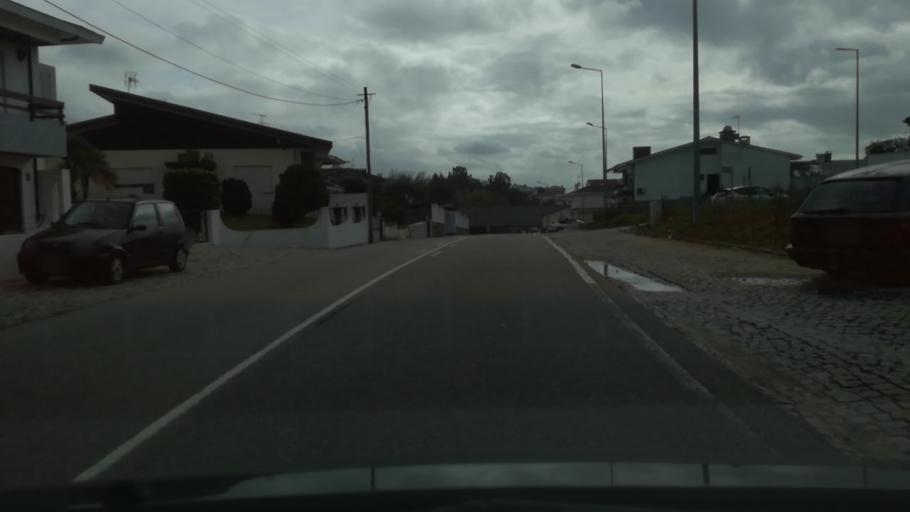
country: PT
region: Porto
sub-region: Maia
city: Maia
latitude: 41.2421
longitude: -8.6344
